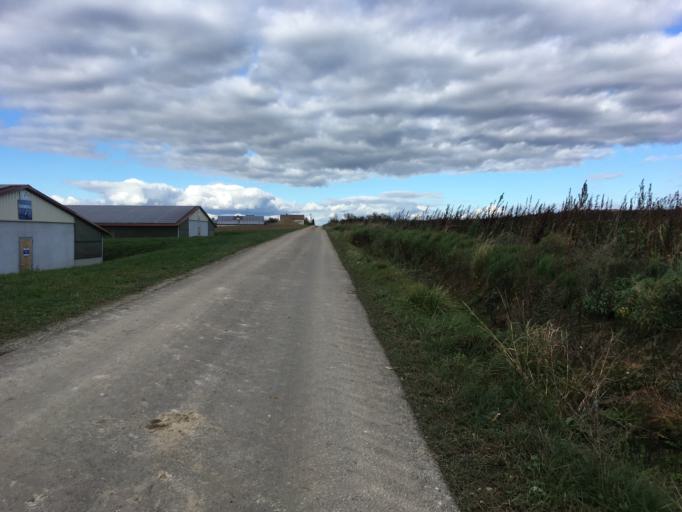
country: DE
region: Baden-Wuerttemberg
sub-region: Regierungsbezirk Stuttgart
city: Kupferzell
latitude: 49.2178
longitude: 9.7290
